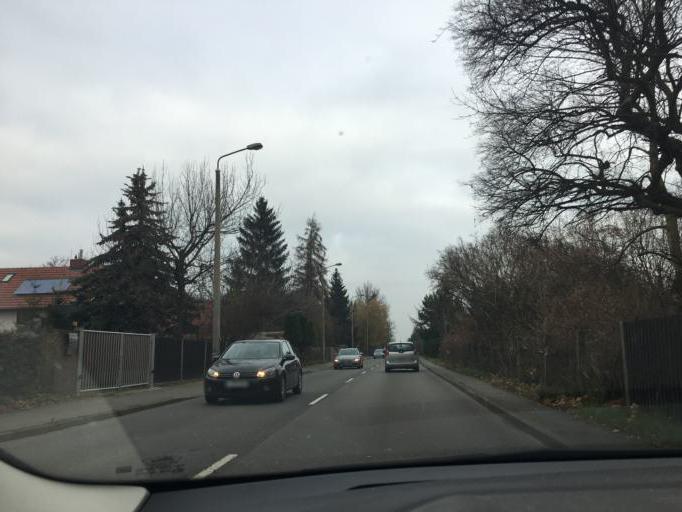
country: DE
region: Saxony
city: Taucha
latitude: 51.3353
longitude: 12.4423
